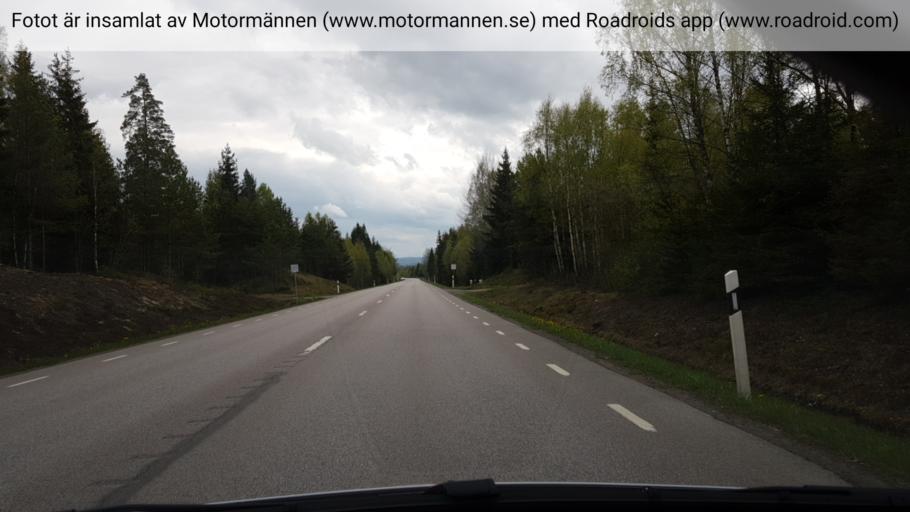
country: SE
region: Vaestra Goetaland
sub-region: Skara Kommun
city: Skara
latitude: 58.3028
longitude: 13.4682
